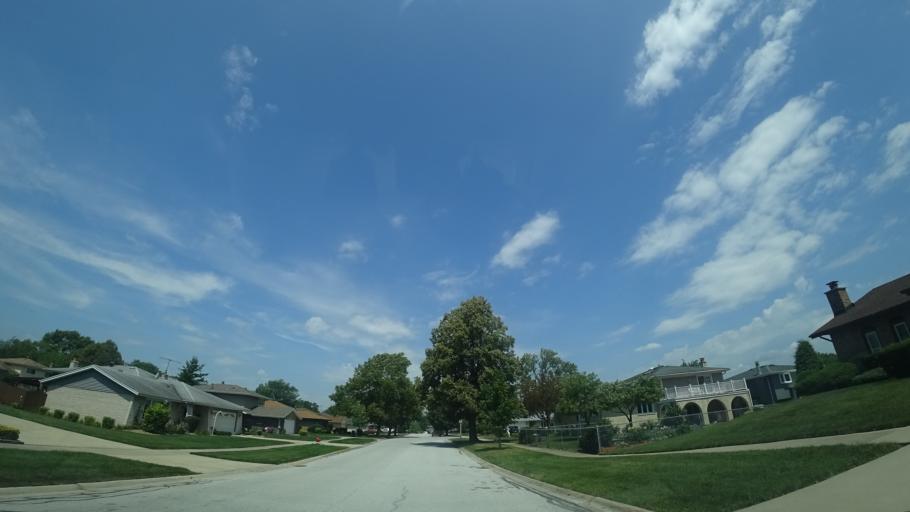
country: US
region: Illinois
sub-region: Cook County
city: Crestwood
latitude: 41.6615
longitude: -87.7668
